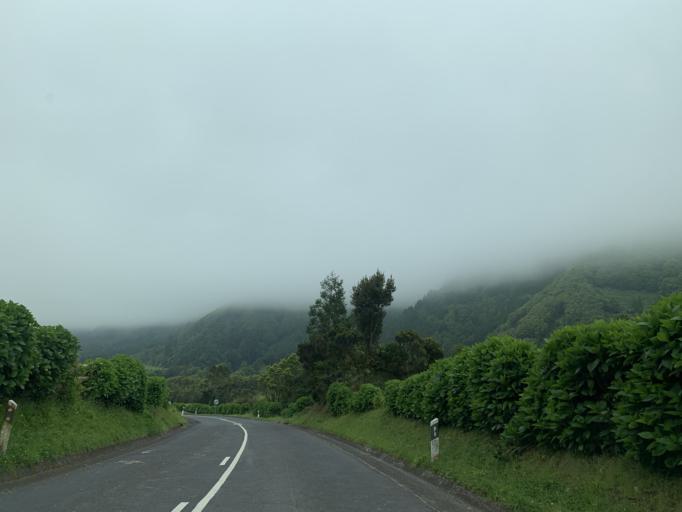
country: PT
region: Azores
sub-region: Ponta Delgada
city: Arrifes
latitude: 37.8672
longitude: -25.8105
